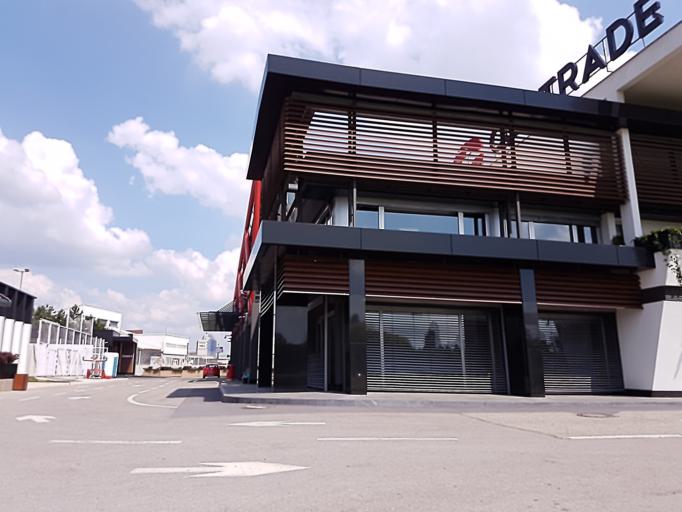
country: RS
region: Central Serbia
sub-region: Belgrade
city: Novi Beograd
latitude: 44.8022
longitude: 20.4192
